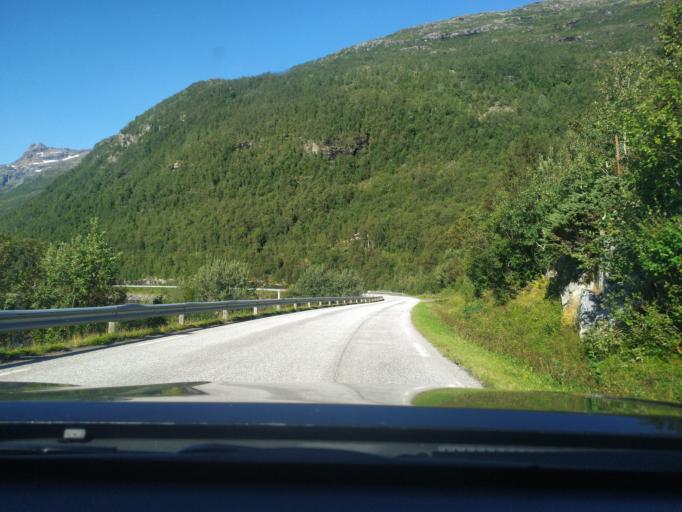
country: NO
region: Troms
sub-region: Dyroy
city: Brostadbotn
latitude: 68.9335
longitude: 17.7028
